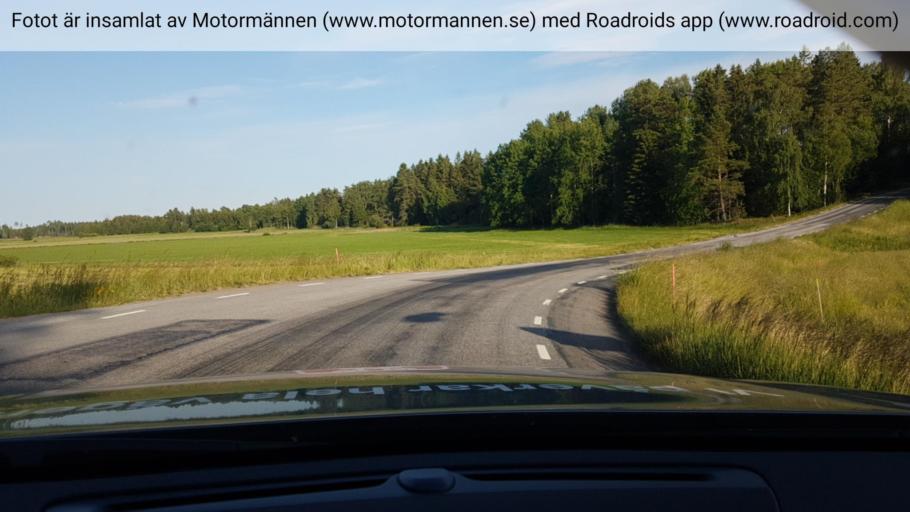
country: SE
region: Uppsala
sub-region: Osthammars Kommun
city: Gimo
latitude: 59.9867
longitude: 18.0604
